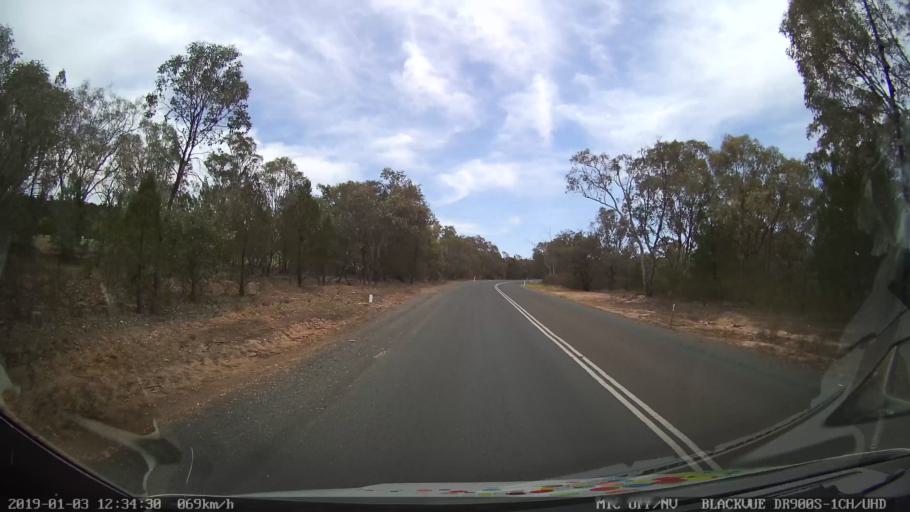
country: AU
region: New South Wales
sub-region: Weddin
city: Grenfell
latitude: -33.8758
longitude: 148.1664
